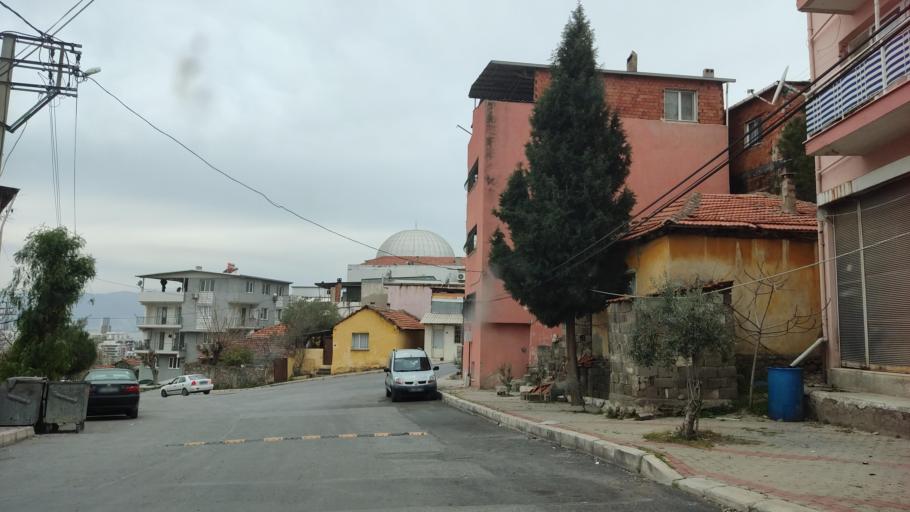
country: TR
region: Izmir
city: Karsiyaka
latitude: 38.4950
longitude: 27.0736
